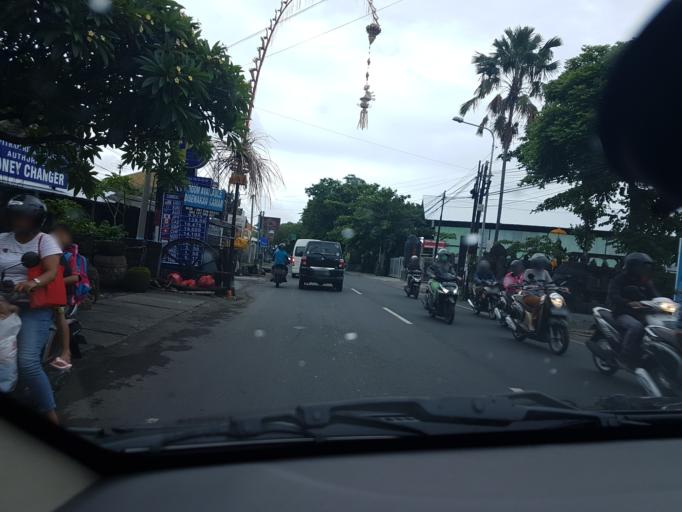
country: ID
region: Bali
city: Kuta
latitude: -8.6704
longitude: 115.1647
